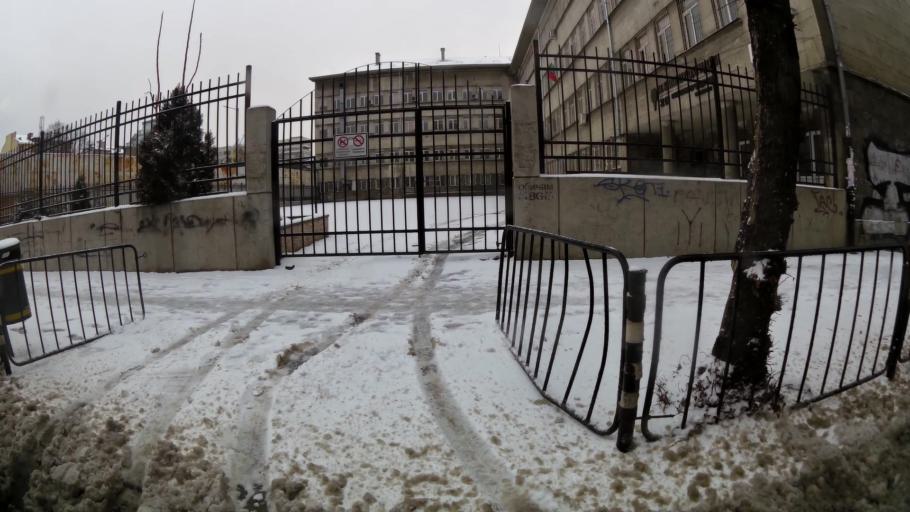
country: BG
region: Sofia-Capital
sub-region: Stolichna Obshtina
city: Sofia
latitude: 42.6992
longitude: 23.3156
